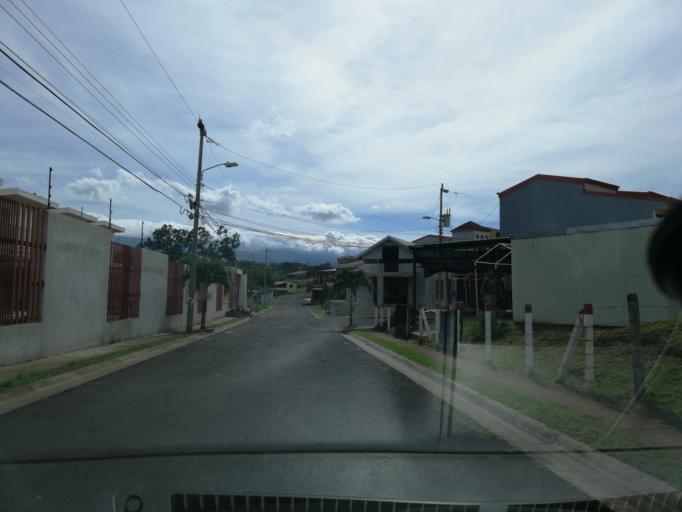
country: CR
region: Alajuela
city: Alajuela
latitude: 10.0136
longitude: -84.1955
